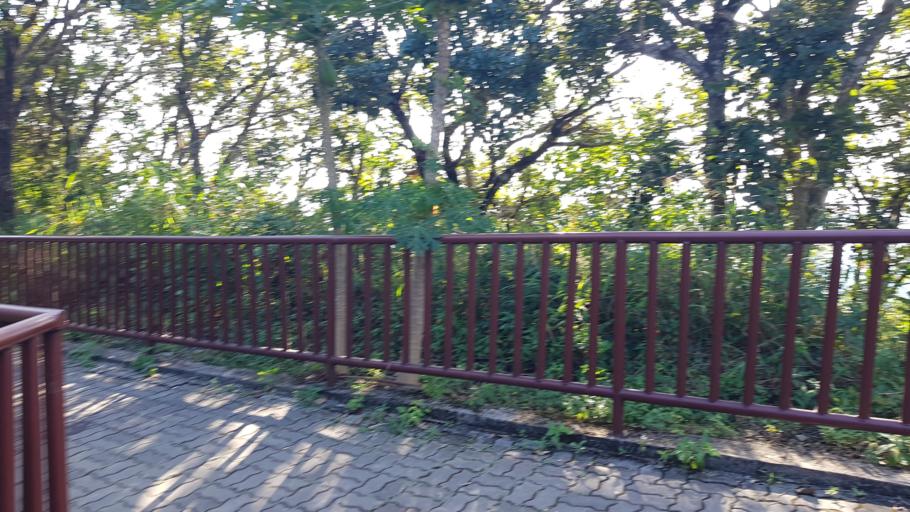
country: TH
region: Chiang Rai
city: Mae Fa Luang
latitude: 20.3227
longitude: 99.8339
